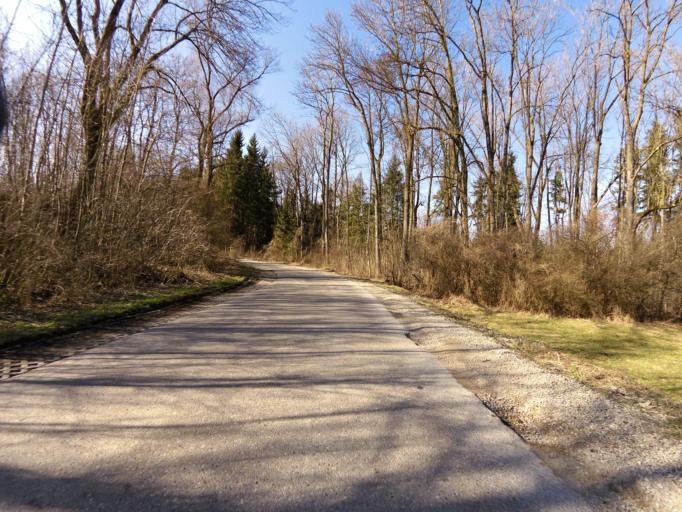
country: DE
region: Bavaria
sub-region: Upper Bavaria
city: Wang
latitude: 48.4910
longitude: 11.9839
